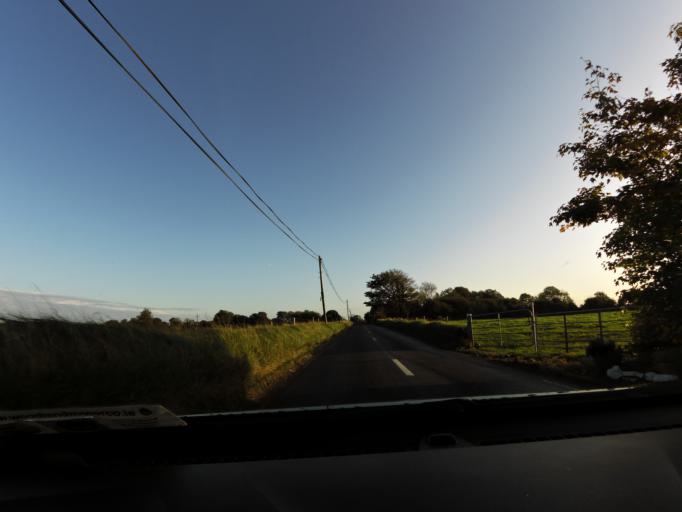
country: IE
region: Connaught
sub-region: Roscommon
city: Castlerea
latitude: 53.6944
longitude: -8.5689
